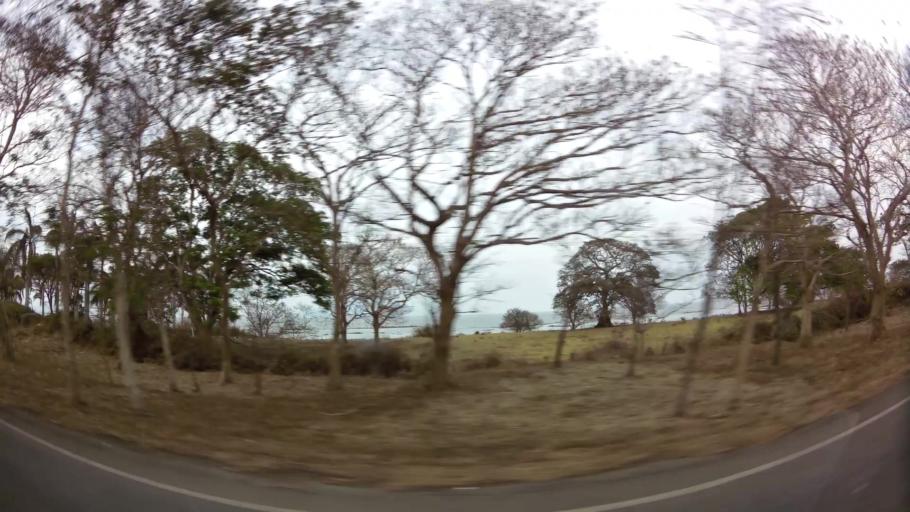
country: NI
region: Rivas
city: San Juan del Sur
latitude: 11.3015
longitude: -85.6903
